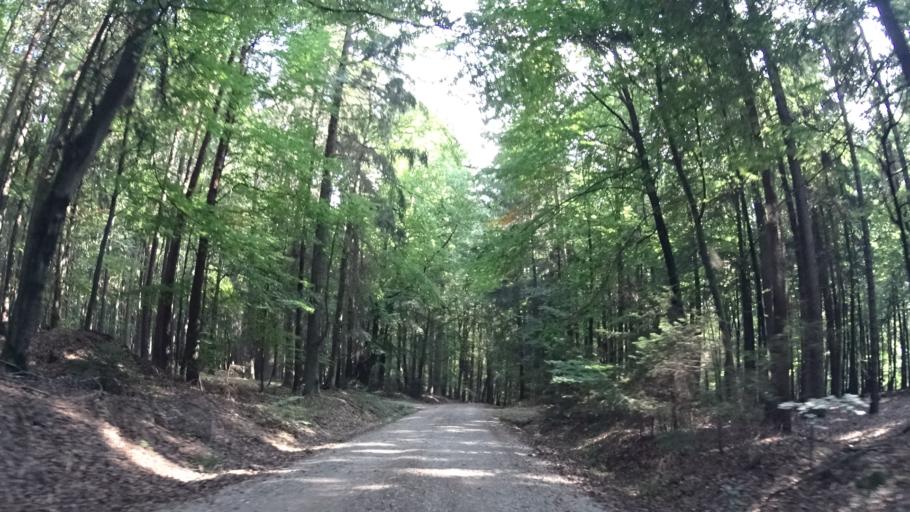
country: DE
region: Bavaria
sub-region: Lower Bavaria
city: Riedenburg
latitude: 48.9742
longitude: 11.6726
